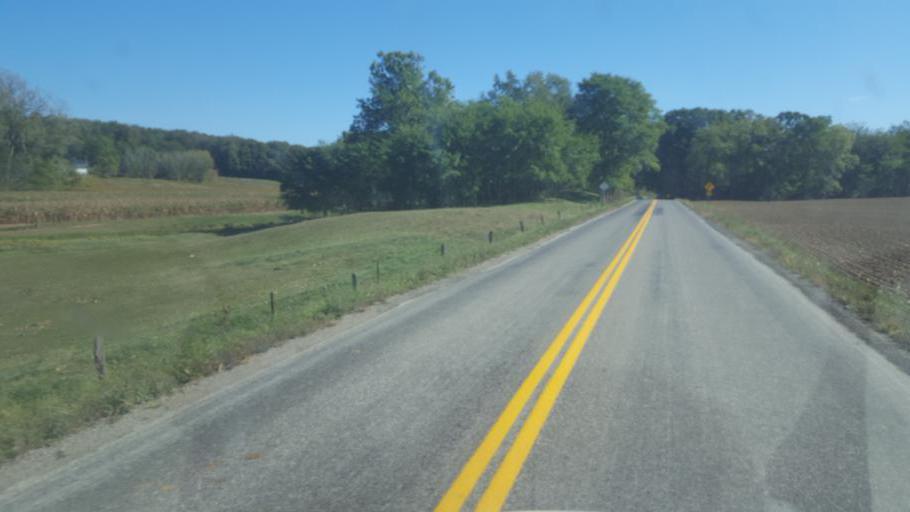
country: US
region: Ohio
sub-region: Wayne County
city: West Salem
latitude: 40.9099
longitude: -82.1595
